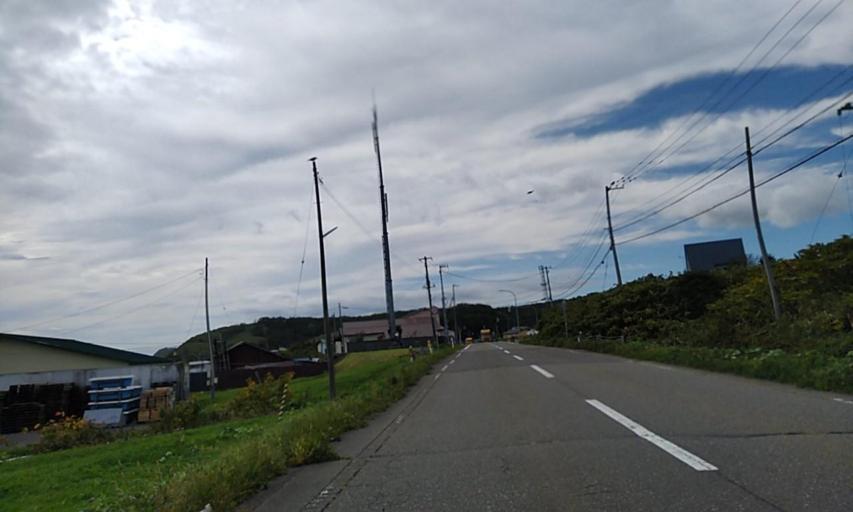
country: JP
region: Hokkaido
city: Kushiro
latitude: 42.8083
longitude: 143.8205
